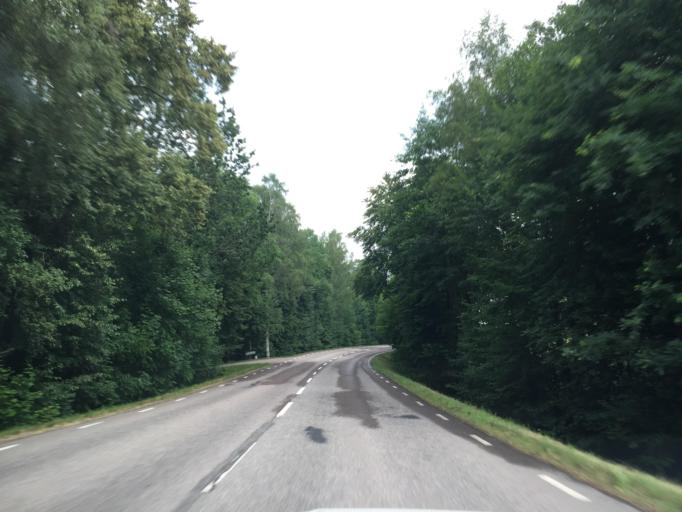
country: SE
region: Vaestra Goetaland
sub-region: Alingsas Kommun
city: Alingsas
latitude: 57.8593
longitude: 12.5597
